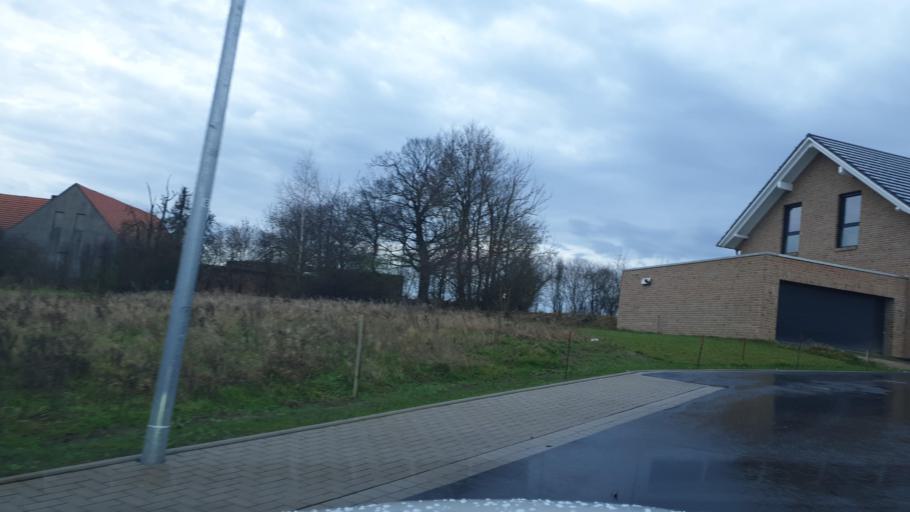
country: DE
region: North Rhine-Westphalia
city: Bad Oeynhausen
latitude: 52.1859
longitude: 8.8176
